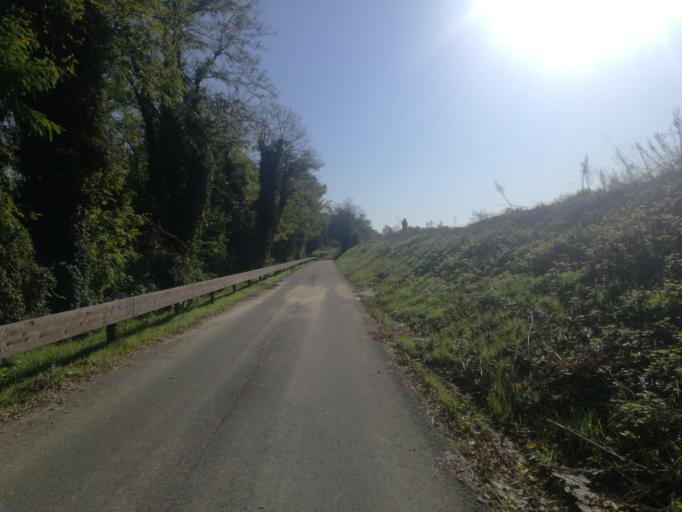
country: IT
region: Lombardy
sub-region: Provincia di Bergamo
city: Bottanuco
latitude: 45.6278
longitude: 9.4987
